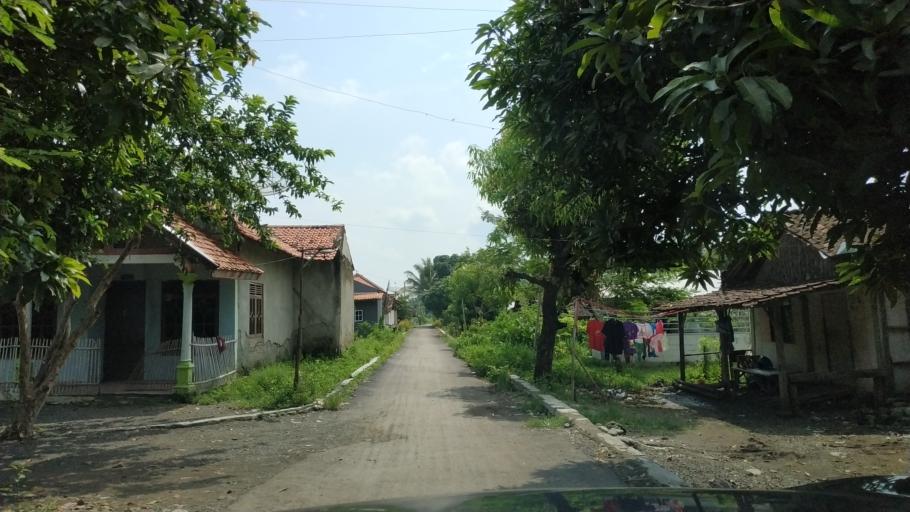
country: ID
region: Central Java
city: Margasari
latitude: -7.0948
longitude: 108.9745
